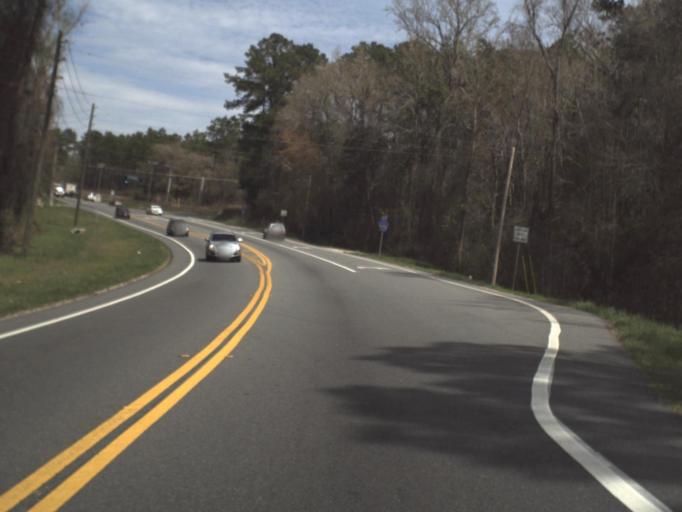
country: US
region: Florida
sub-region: Gadsden County
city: Midway
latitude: 30.4910
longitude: -84.3617
